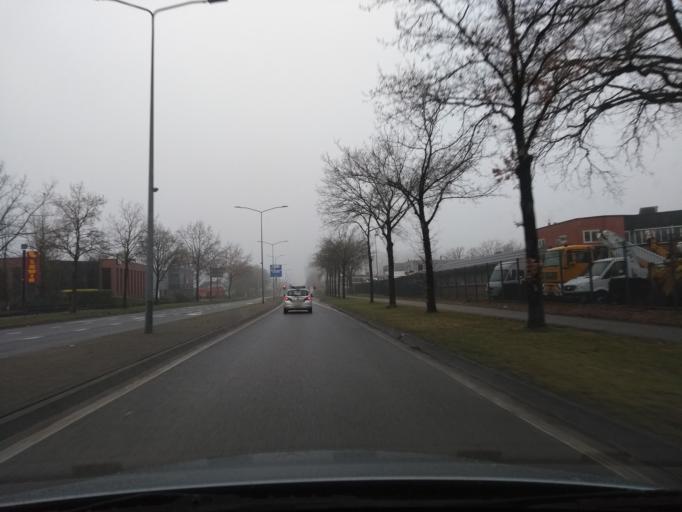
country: NL
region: Overijssel
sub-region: Gemeente Almelo
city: Almelo
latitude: 52.3740
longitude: 6.6514
